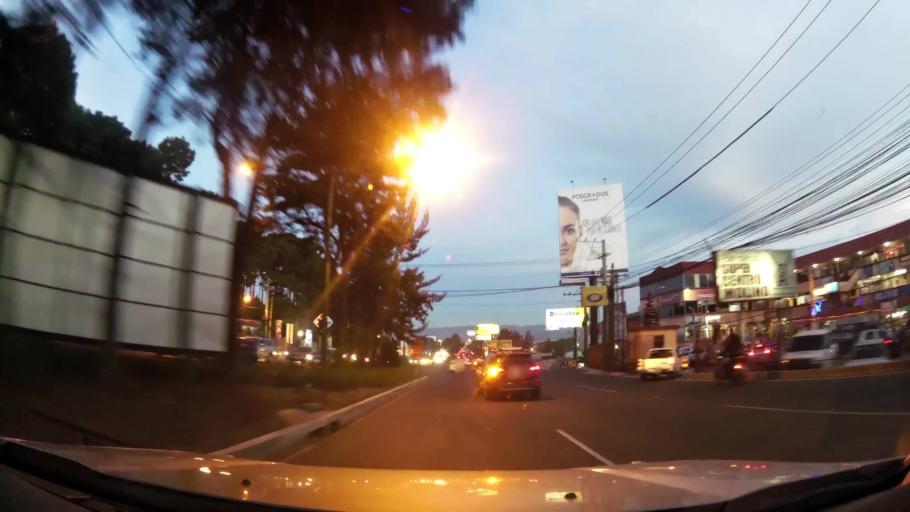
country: GT
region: Guatemala
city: Mixco
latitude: 14.6347
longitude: -90.5924
